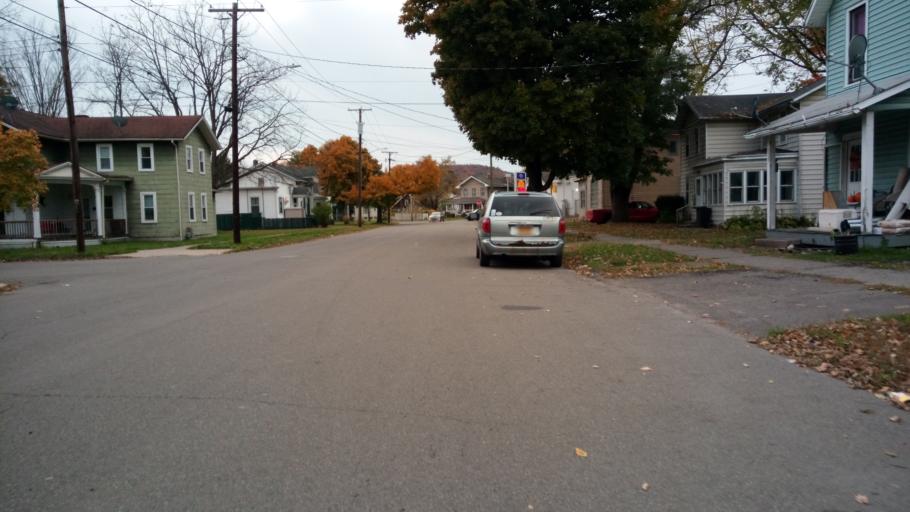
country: US
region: New York
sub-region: Chemung County
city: Elmira
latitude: 42.0736
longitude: -76.8034
